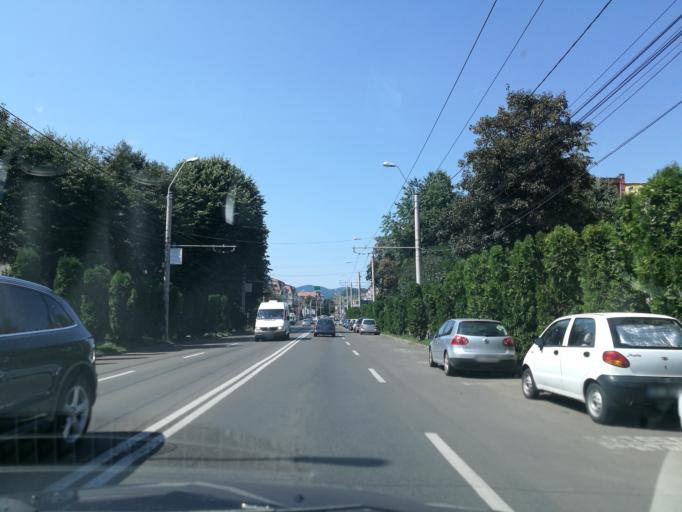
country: RO
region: Neamt
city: Piatra Neamt
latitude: 46.9351
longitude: 26.3548
